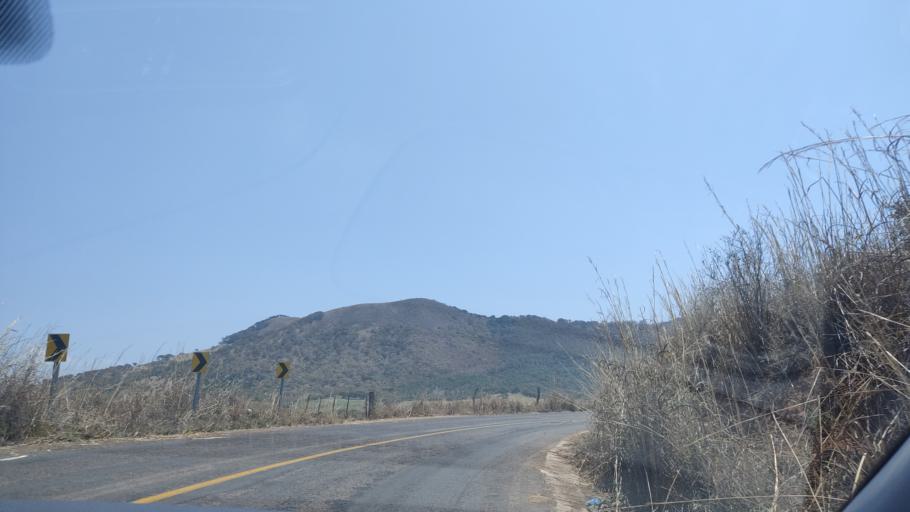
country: MX
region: Nayarit
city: Puga
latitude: 21.5768
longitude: -104.7584
